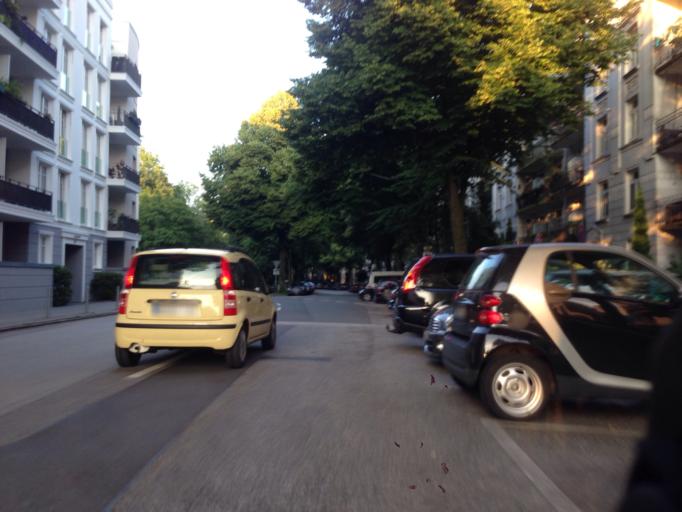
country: DE
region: Hamburg
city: Stellingen
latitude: 53.5820
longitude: 9.9415
